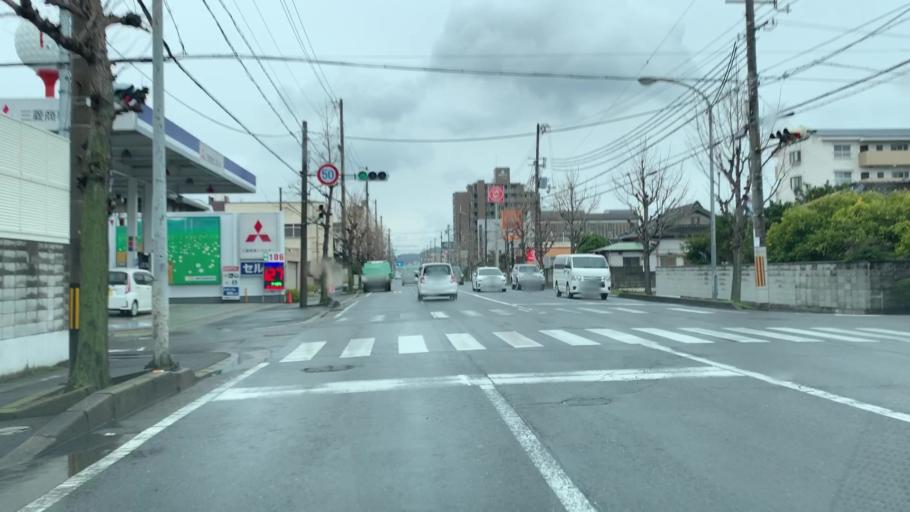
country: JP
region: Wakayama
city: Wakayama-shi
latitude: 34.2232
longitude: 135.1596
